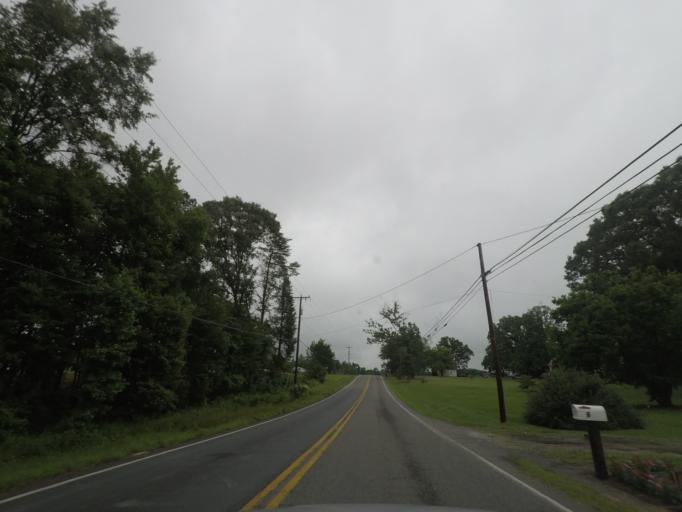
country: US
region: Virginia
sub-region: Fluvanna County
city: Weber City
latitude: 37.7727
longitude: -78.2527
